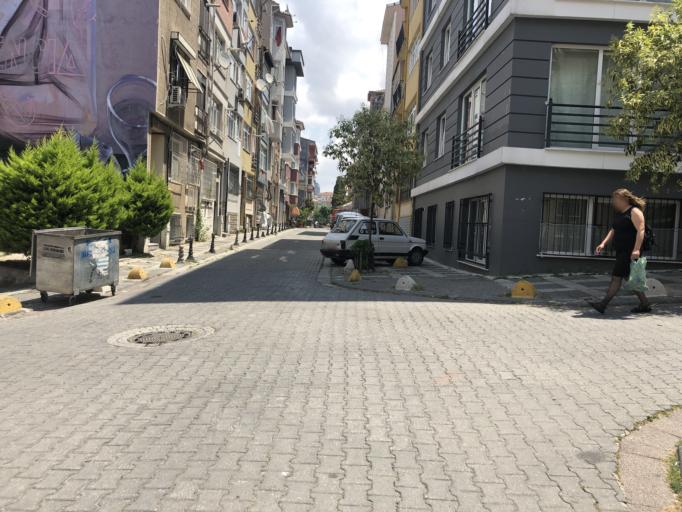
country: TR
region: Istanbul
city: UEskuedar
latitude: 40.9970
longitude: 29.0281
